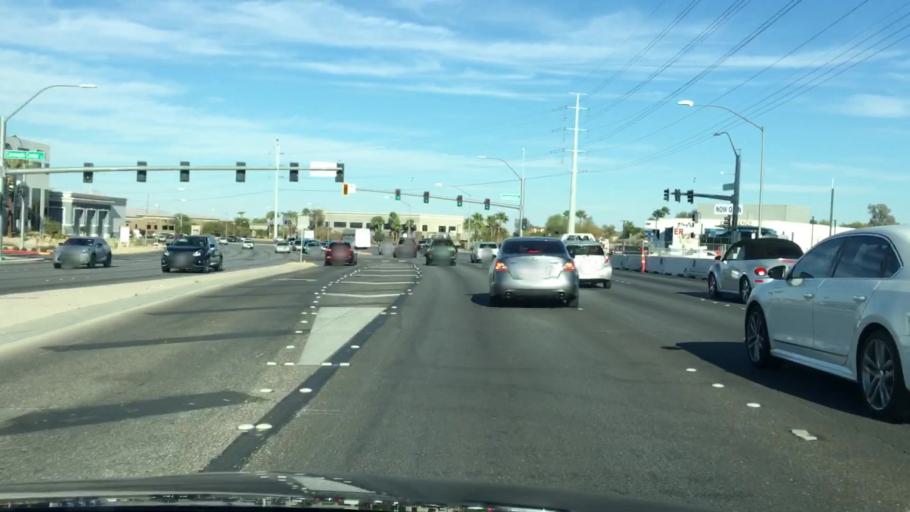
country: US
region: Nevada
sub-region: Clark County
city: Whitney
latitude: 36.0153
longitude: -115.1026
